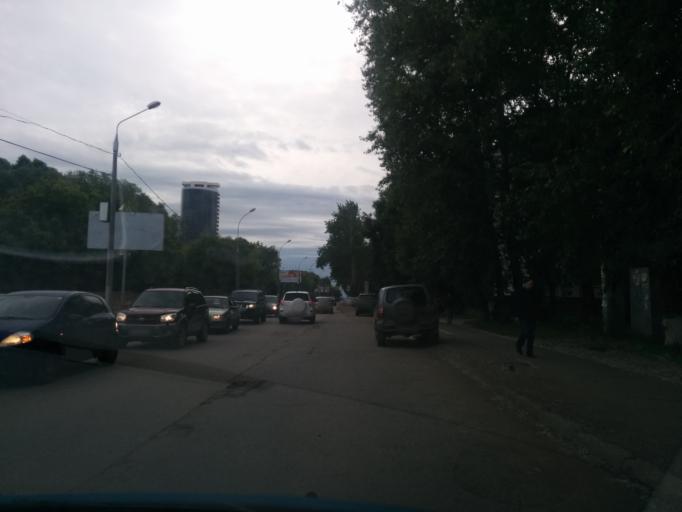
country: RU
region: Perm
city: Perm
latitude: 58.0094
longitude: 56.2934
